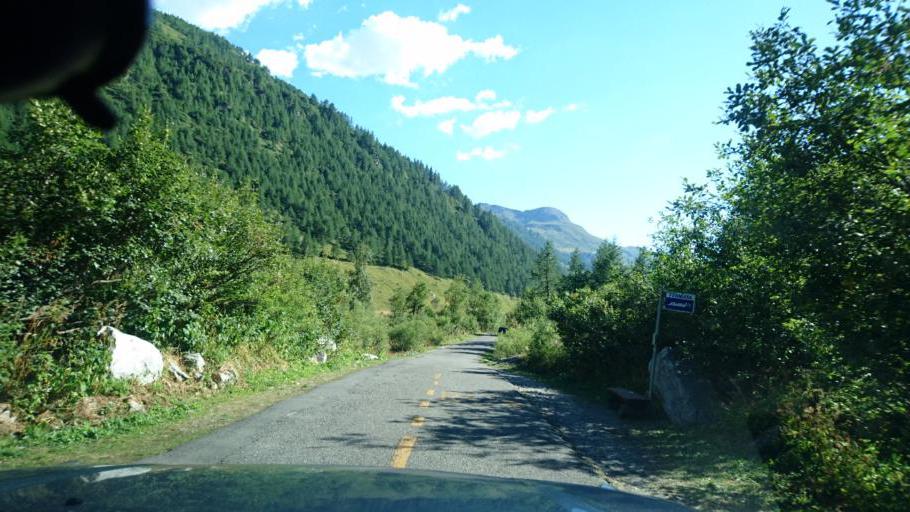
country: IT
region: Aosta Valley
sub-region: Valle d'Aosta
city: Courmayeur
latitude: 45.8624
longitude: 7.0375
